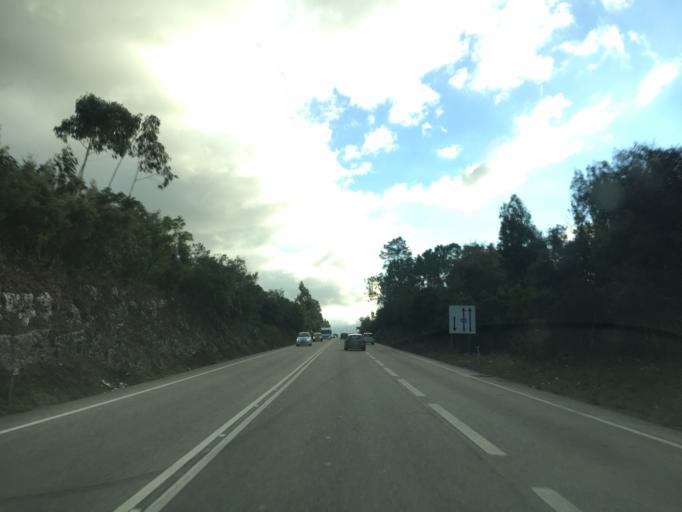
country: PT
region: Leiria
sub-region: Alcobaca
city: Aljubarrota
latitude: 39.5756
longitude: -8.8752
